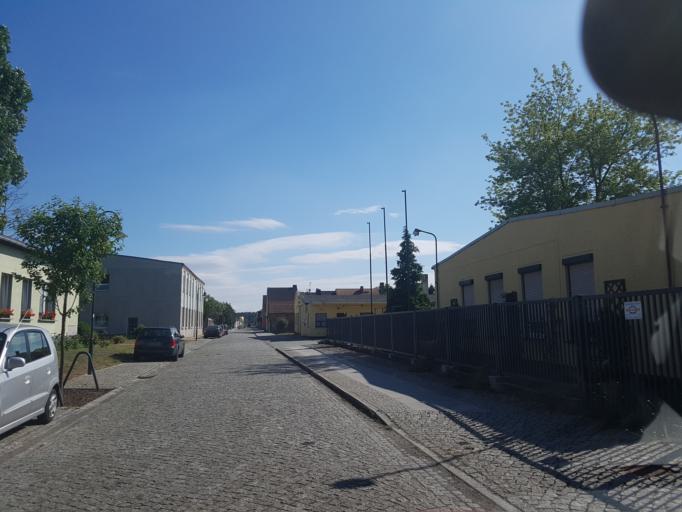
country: DE
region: Brandenburg
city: Juterbog
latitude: 52.0229
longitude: 13.1081
